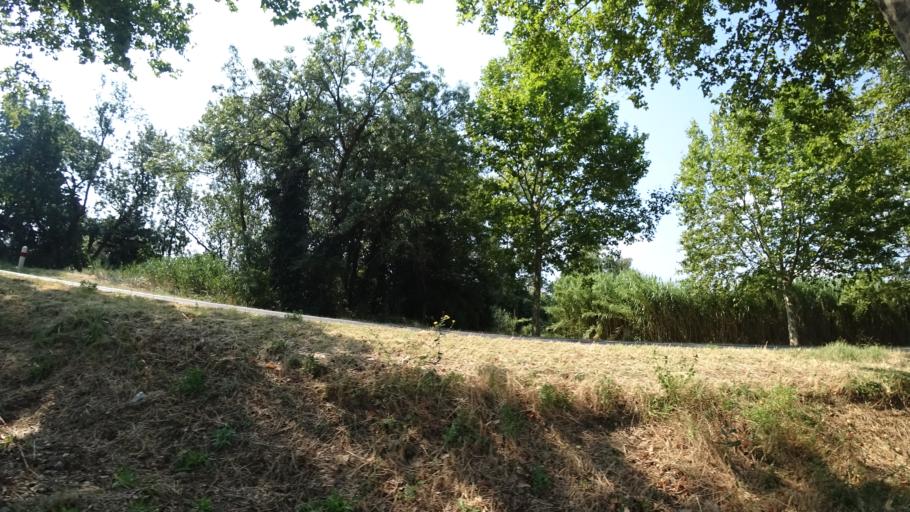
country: FR
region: Languedoc-Roussillon
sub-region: Departement des Pyrenees-Orientales
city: Villelongue-de-la-Salanque
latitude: 42.7261
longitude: 2.9670
